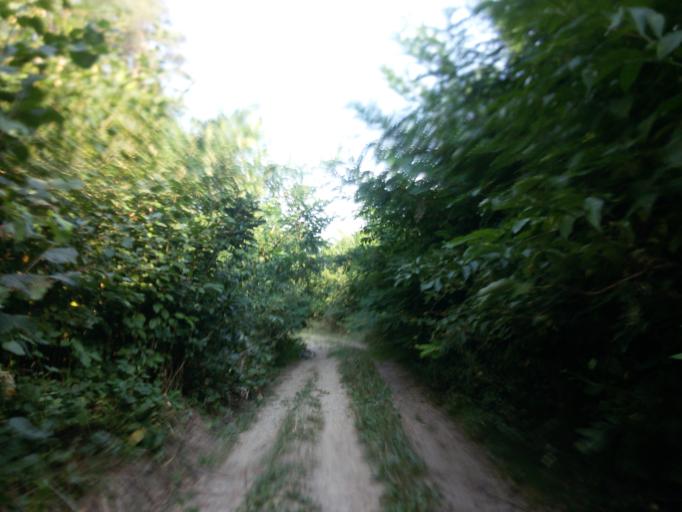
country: CZ
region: South Moravian
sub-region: Okres Brno-Venkov
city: Lelekovice
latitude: 49.2754
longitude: 16.5640
